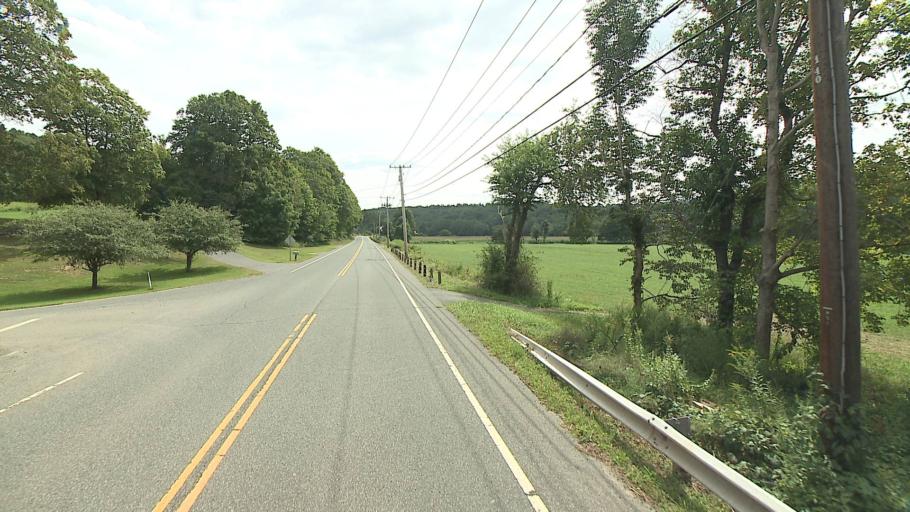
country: US
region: Connecticut
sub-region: Litchfield County
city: Woodbury
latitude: 41.5854
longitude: -73.2308
